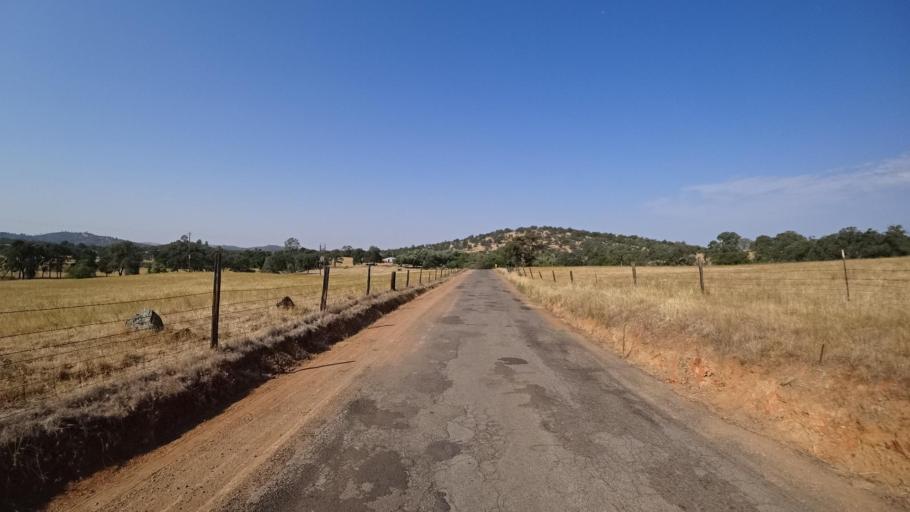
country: US
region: California
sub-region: Tuolumne County
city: Tuolumne City
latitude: 37.7202
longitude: -120.2967
